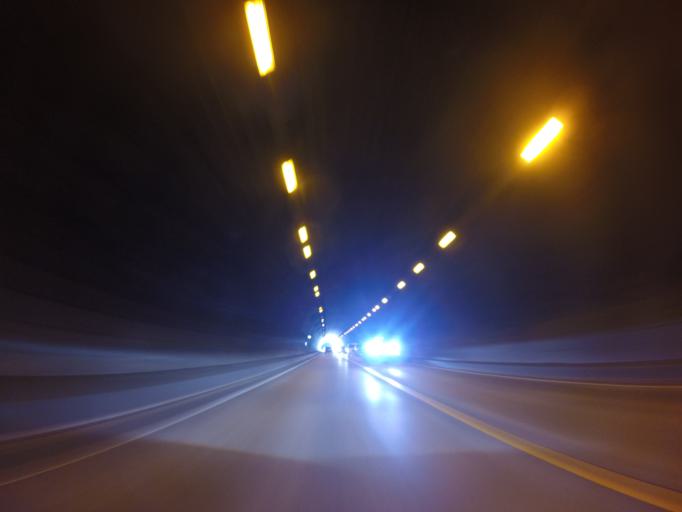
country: JP
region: Shizuoka
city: Mishima
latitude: 35.0330
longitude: 138.9228
